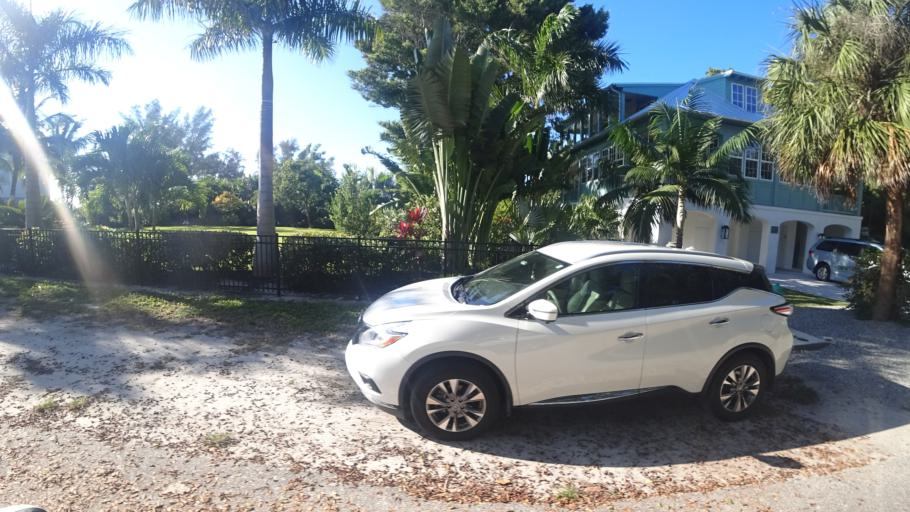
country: US
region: Florida
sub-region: Manatee County
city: Anna Maria
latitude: 27.5211
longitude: -82.7305
